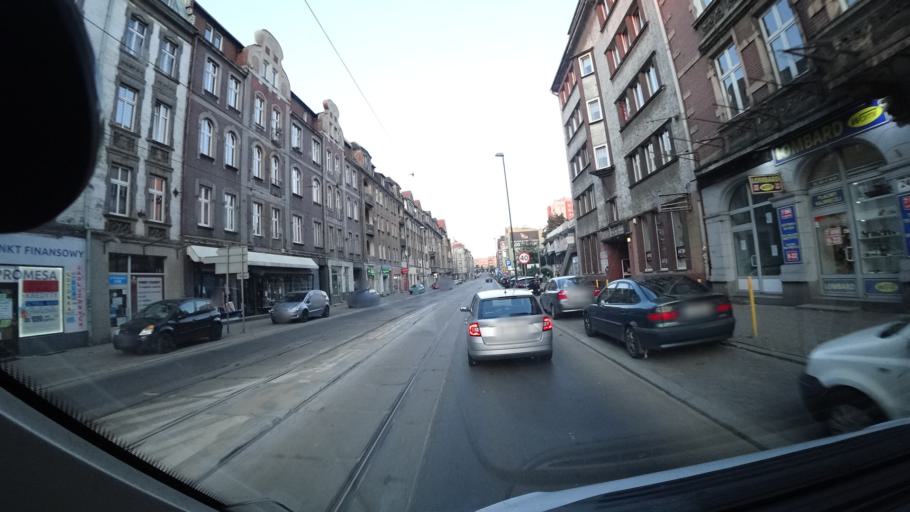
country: PL
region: Silesian Voivodeship
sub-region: Zabrze
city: Zabrze
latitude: 50.3070
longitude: 18.7789
